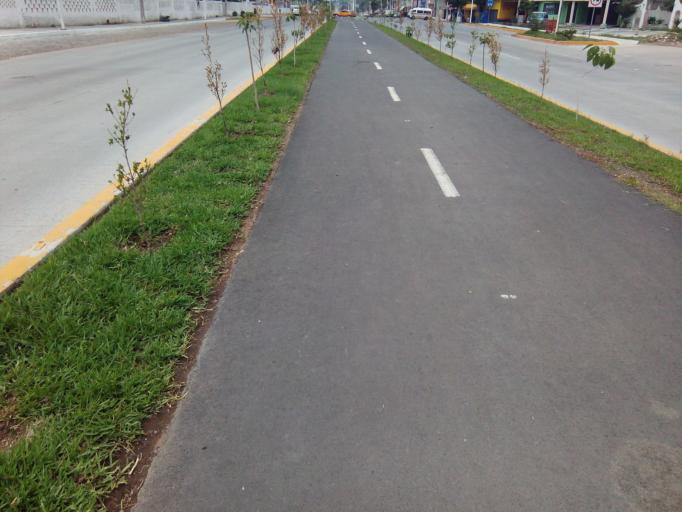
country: MX
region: Nayarit
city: Tepic
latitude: 21.5338
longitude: -104.8743
